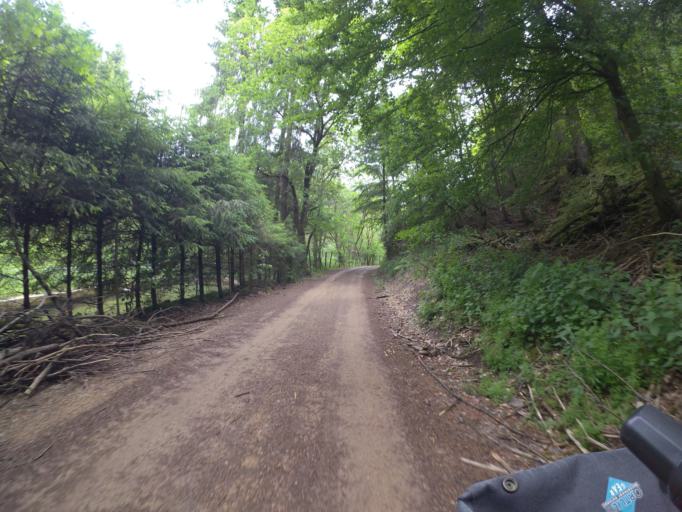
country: DE
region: North Rhine-Westphalia
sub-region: Regierungsbezirk Koln
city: Hellenthal
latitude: 50.4323
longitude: 6.4025
